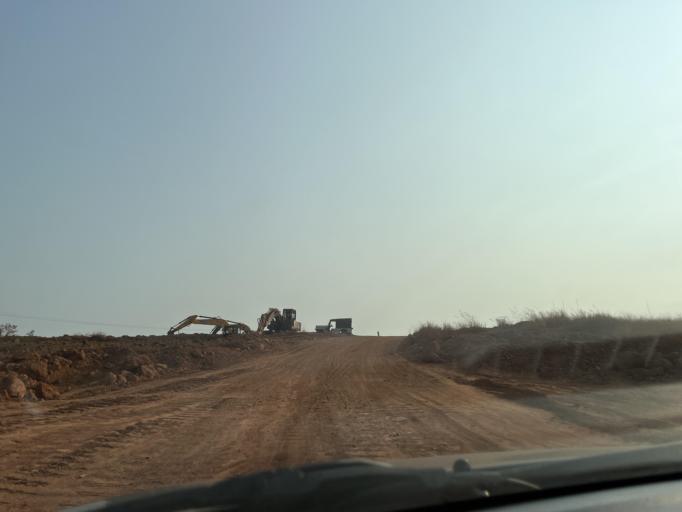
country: IN
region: Goa
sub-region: North Goa
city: Pernem
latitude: 15.6898
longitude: 73.8381
